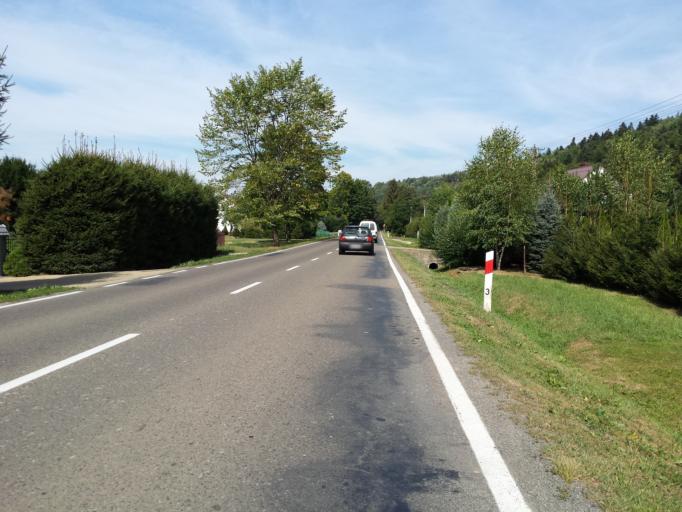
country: PL
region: Subcarpathian Voivodeship
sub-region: Powiat leski
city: Lesko
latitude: 49.4528
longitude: 22.3439
